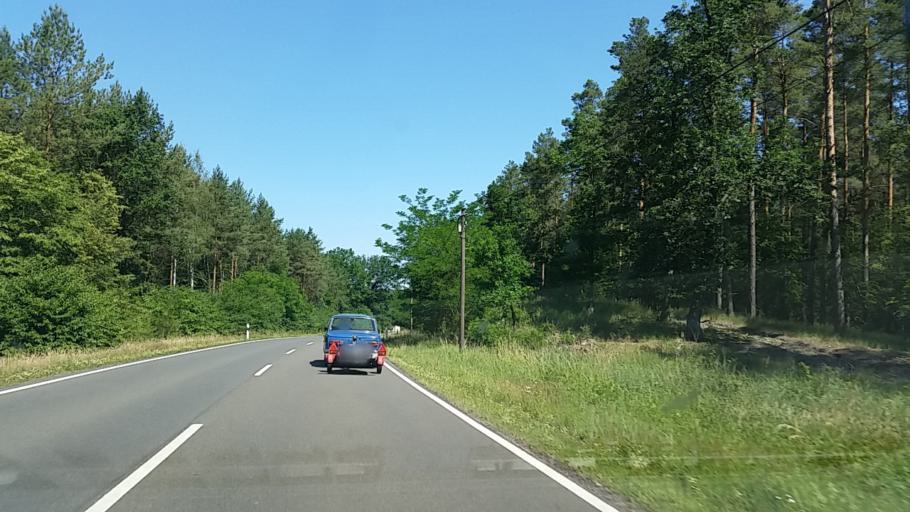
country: DE
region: Saxony-Anhalt
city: Kemberg
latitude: 51.7147
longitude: 12.6184
